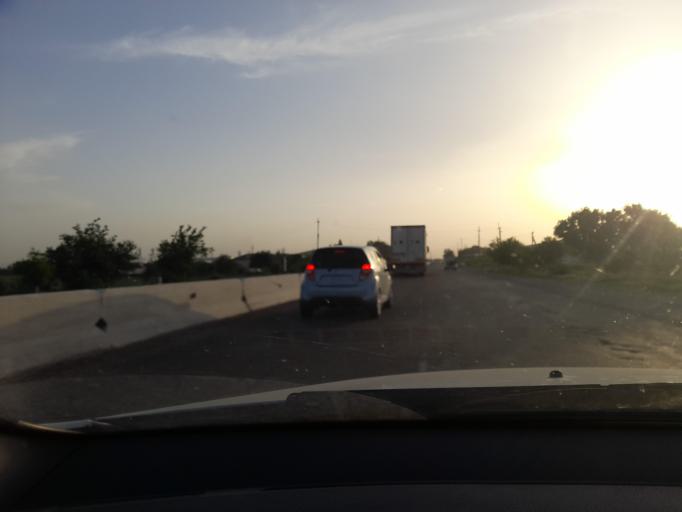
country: UZ
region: Bukhara
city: Ghijduwon
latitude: 40.0859
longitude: 64.6937
